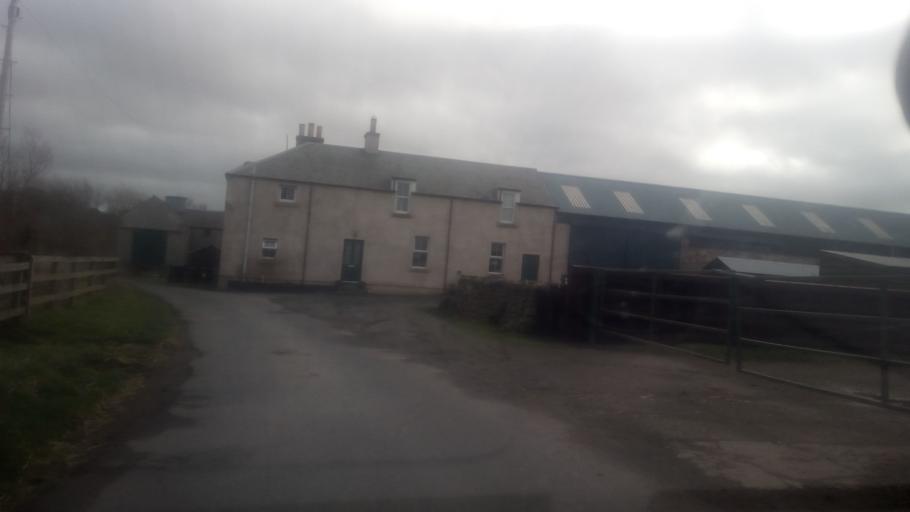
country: GB
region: Scotland
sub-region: The Scottish Borders
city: Kelso
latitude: 55.5434
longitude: -2.4702
